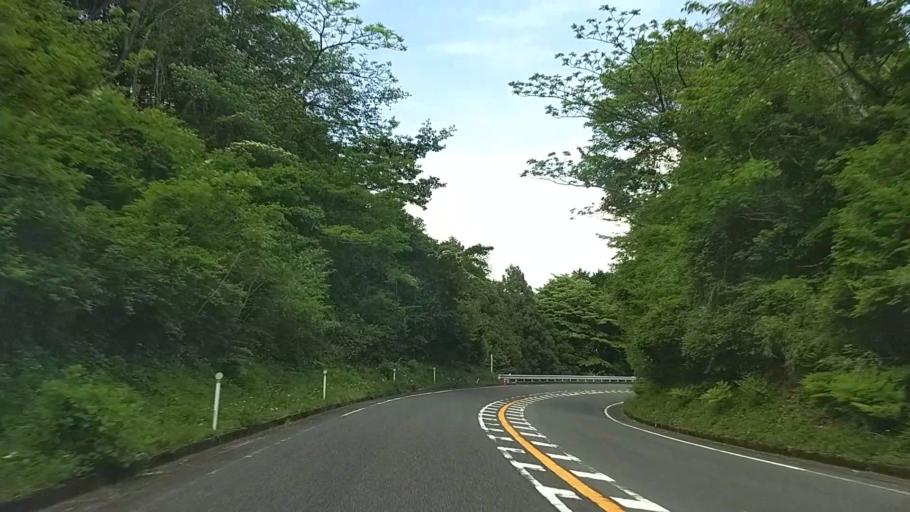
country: JP
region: Kanagawa
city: Odawara
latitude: 35.2166
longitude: 139.1119
